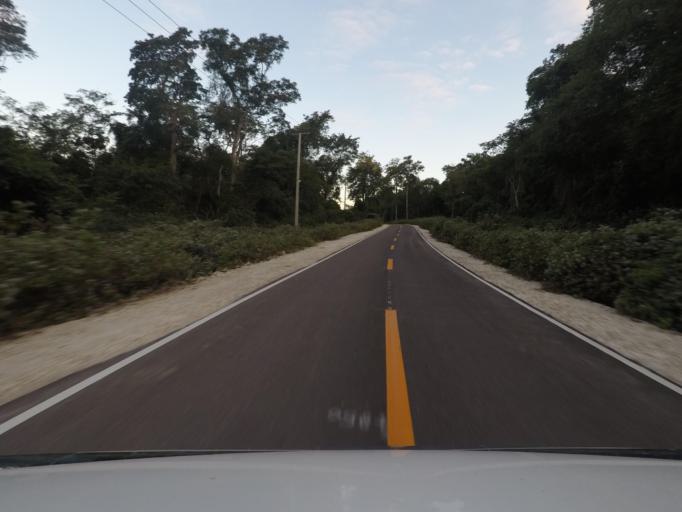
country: TL
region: Lautem
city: Lospalos
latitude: -8.4022
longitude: 127.2888
